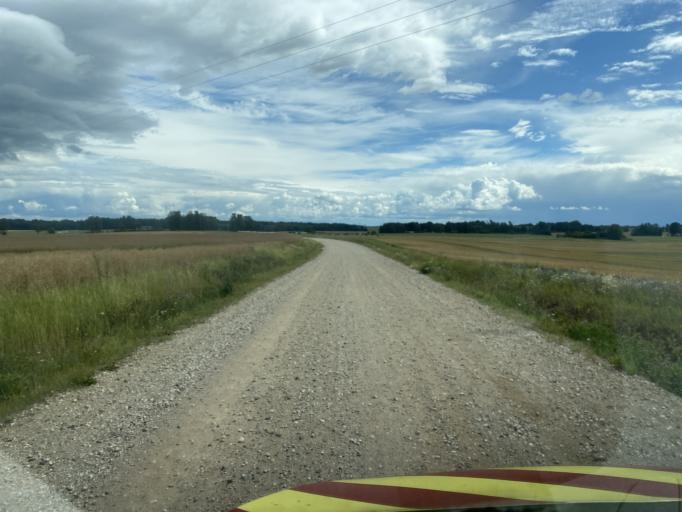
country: EE
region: Valgamaa
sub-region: Torva linn
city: Torva
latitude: 57.9535
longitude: 25.9590
